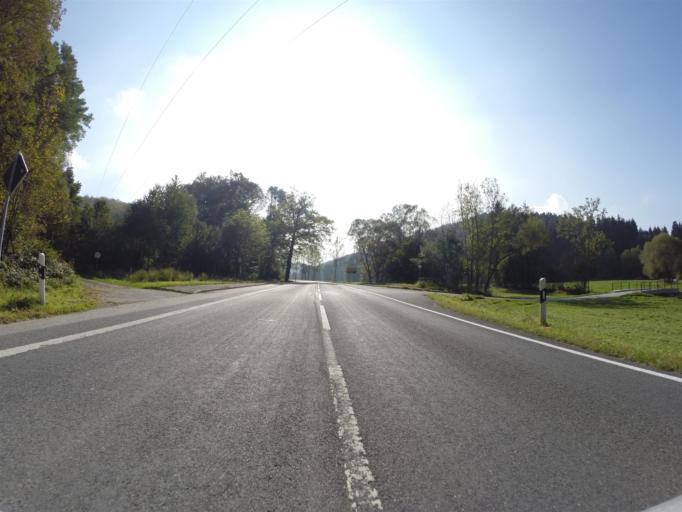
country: DE
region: Thuringia
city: Geisenhain
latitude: 50.8243
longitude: 11.7127
